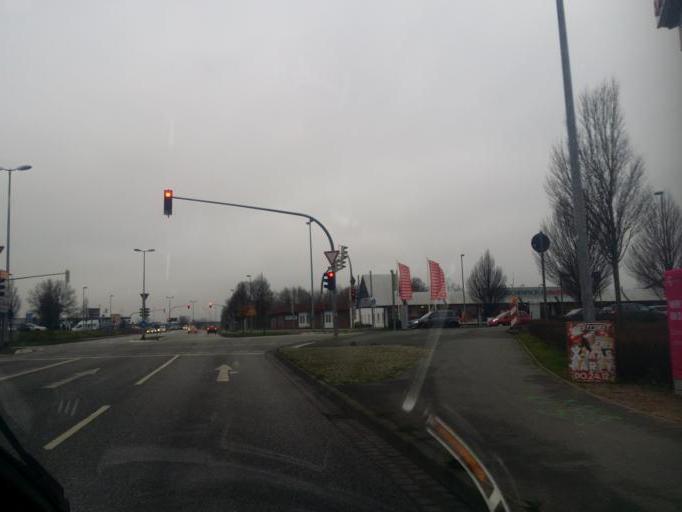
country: DE
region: Schleswig-Holstein
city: Heide
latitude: 54.1981
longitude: 9.1244
